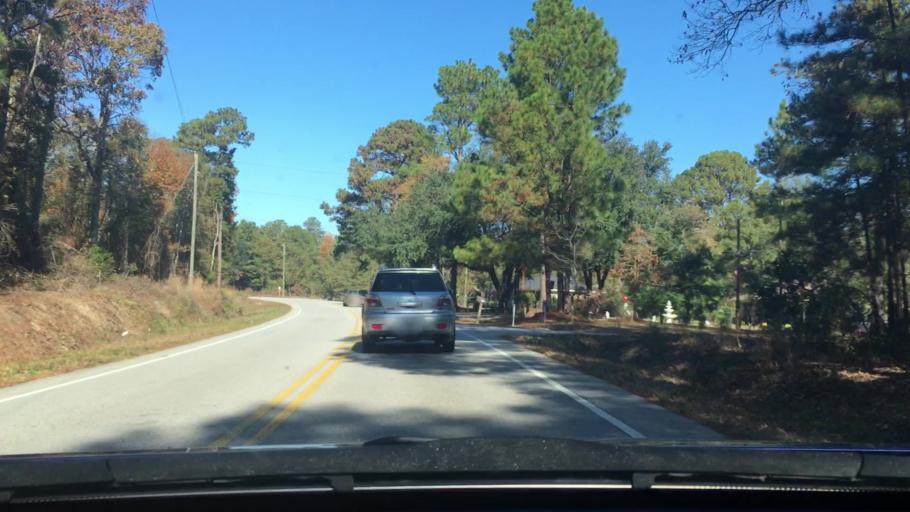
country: US
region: South Carolina
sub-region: Sumter County
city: South Sumter
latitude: 33.8849
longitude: -80.3635
